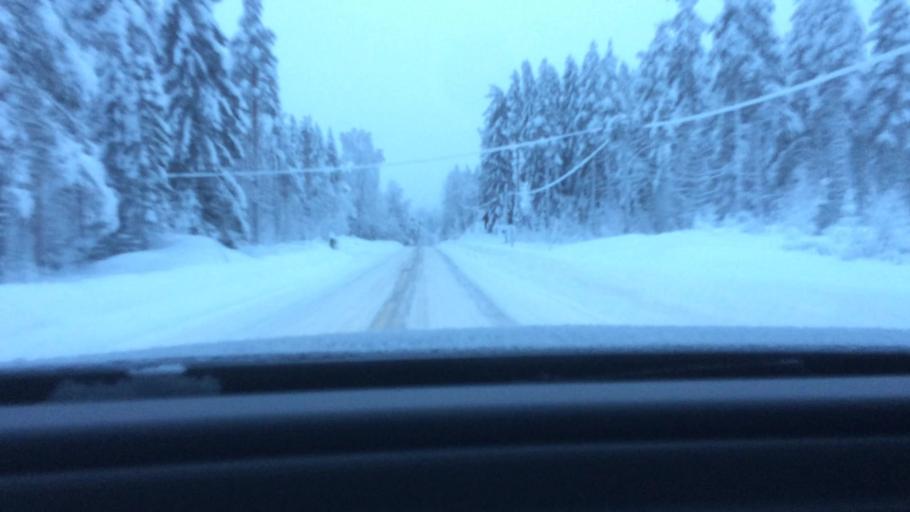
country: SE
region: Gaevleborg
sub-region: Ljusdals Kommun
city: Farila
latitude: 61.7656
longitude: 15.1542
